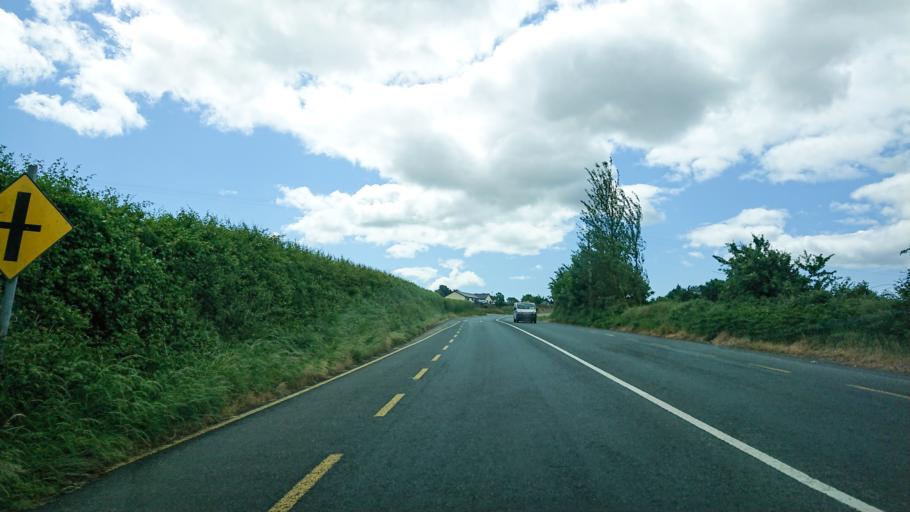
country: IE
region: Munster
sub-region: Waterford
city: Tra Mhor
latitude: 52.2241
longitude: -7.1998
